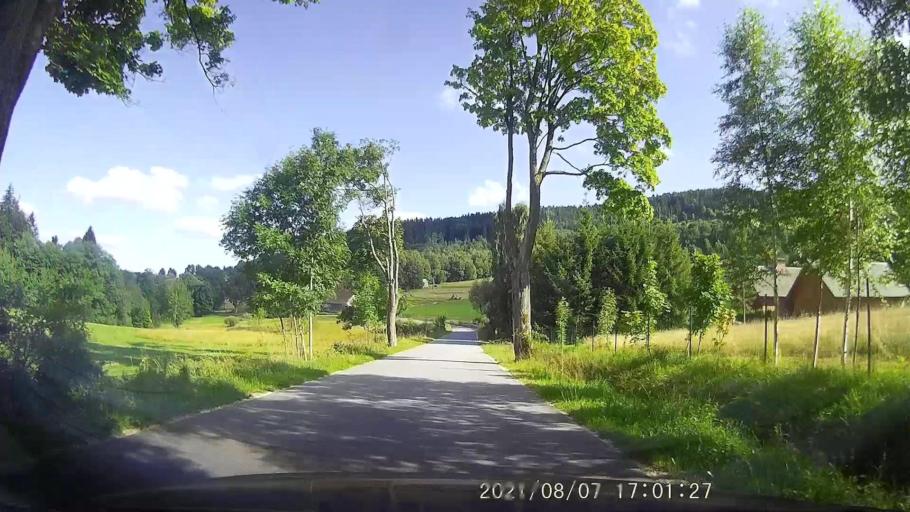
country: PL
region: Lower Silesian Voivodeship
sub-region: Powiat klodzki
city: Bystrzyca Klodzka
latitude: 50.2874
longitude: 16.5532
